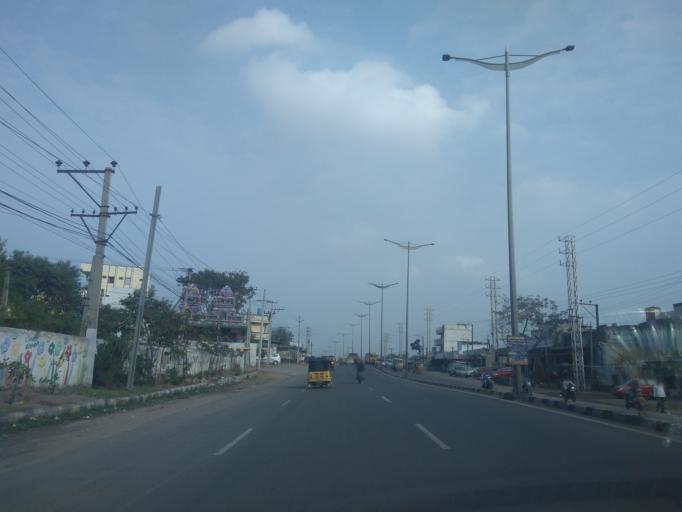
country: IN
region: Telangana
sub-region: Rangareddi
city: Balapur
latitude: 17.3162
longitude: 78.4543
